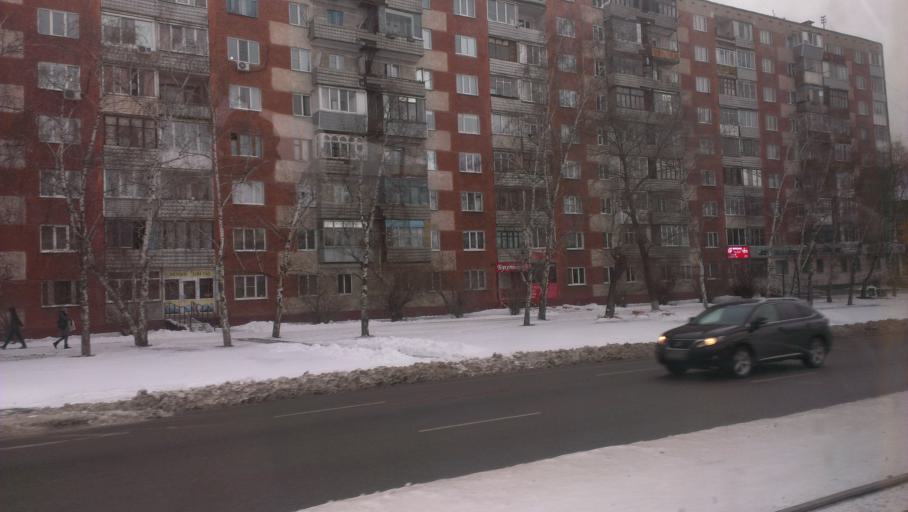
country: RU
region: Altai Krai
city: Novosilikatnyy
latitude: 53.3678
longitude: 83.6770
